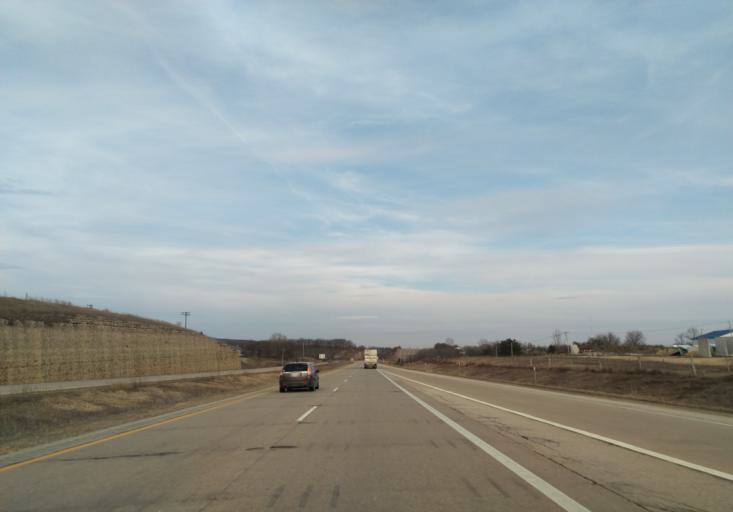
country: US
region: Wisconsin
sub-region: Iowa County
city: Barneveld
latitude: 43.0099
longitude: -89.8961
